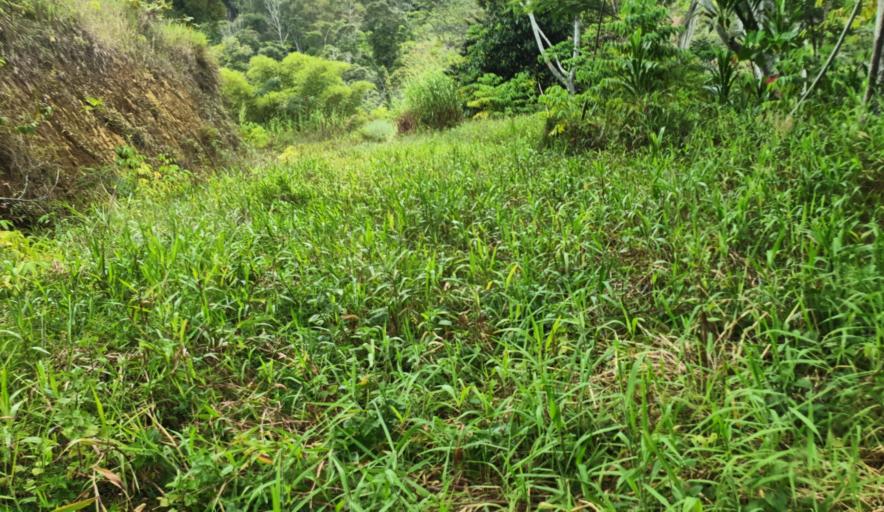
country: PG
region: Jiwaka
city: Minj
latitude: -5.9143
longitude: 144.8271
